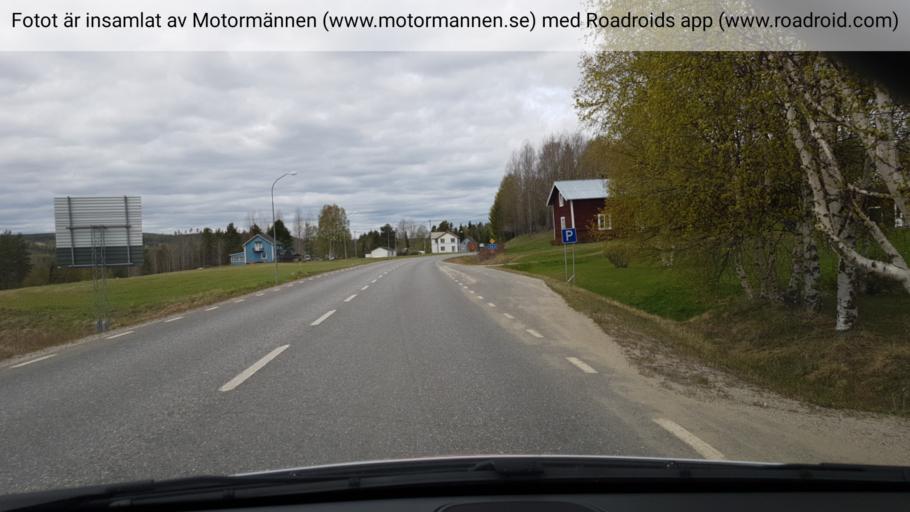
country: SE
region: Vaesterbotten
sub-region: Mala Kommun
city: Mala
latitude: 64.9873
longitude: 18.5130
